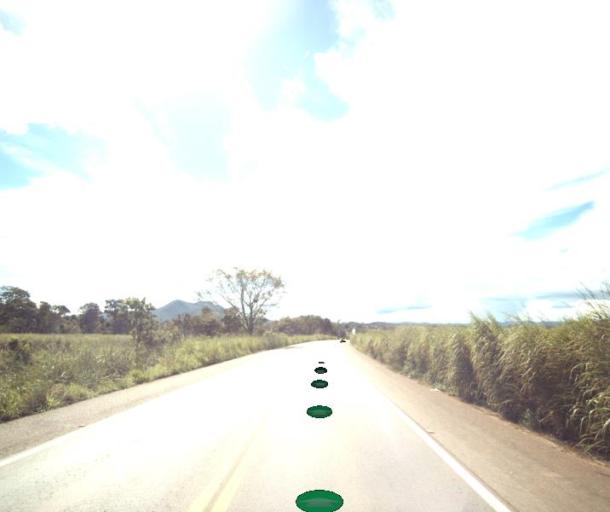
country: BR
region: Goias
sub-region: Jaragua
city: Jaragua
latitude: -15.8556
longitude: -49.2646
